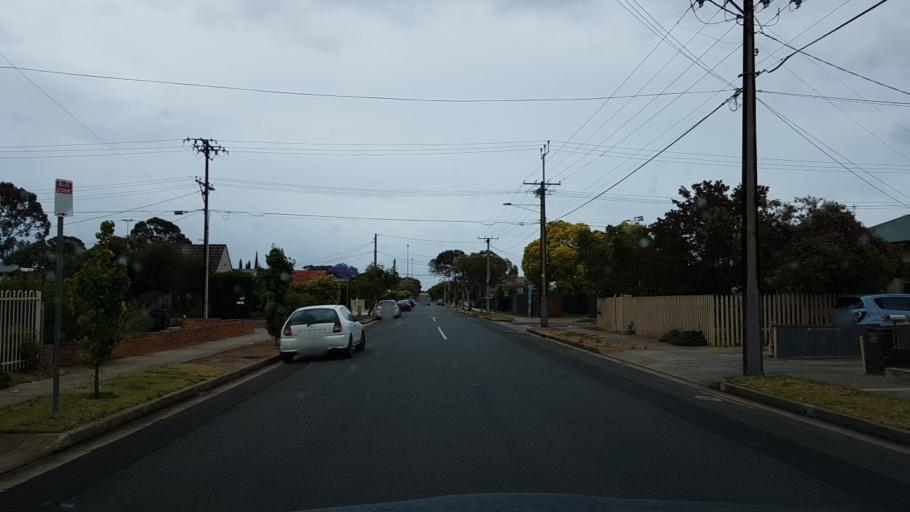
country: AU
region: South Australia
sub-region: Marion
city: South Plympton
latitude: -34.9720
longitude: 138.5517
